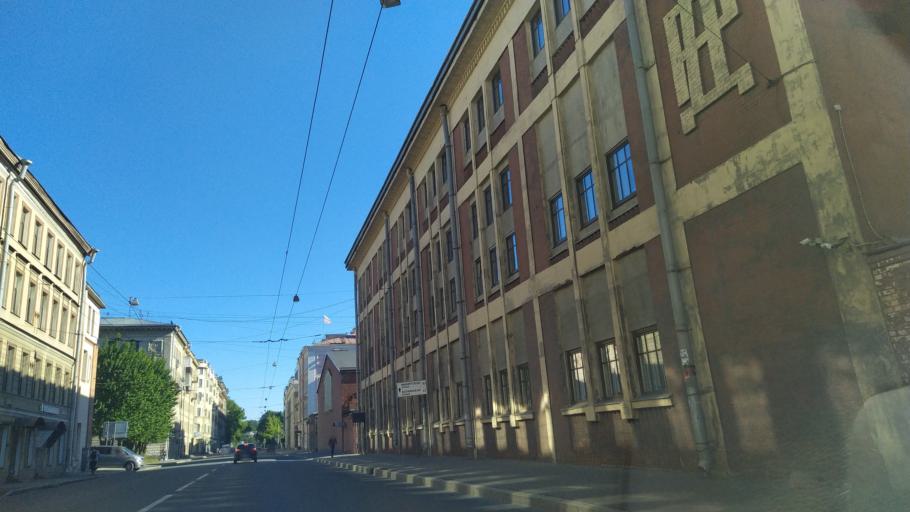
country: RU
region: Leningrad
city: Sampsonievskiy
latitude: 59.9663
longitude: 30.3430
